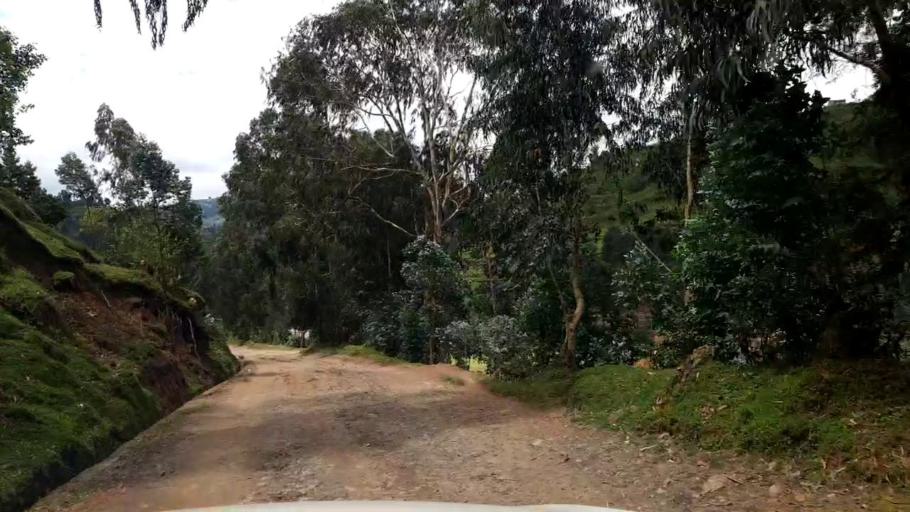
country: RW
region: Western Province
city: Kibuye
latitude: -1.9168
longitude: 29.4578
